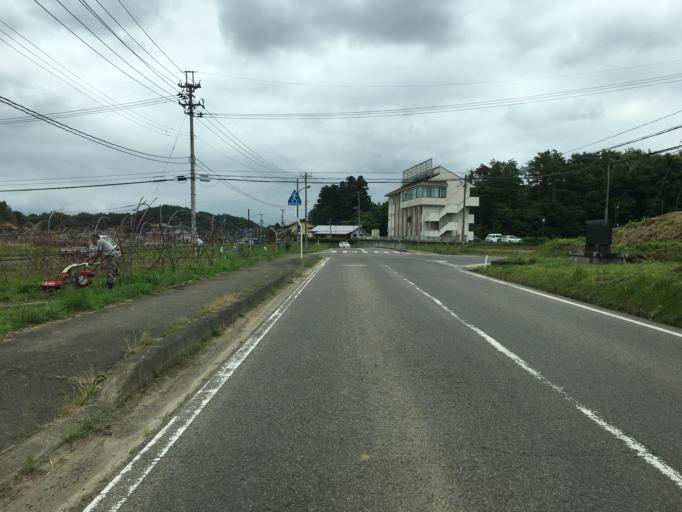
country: JP
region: Fukushima
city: Nihommatsu
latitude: 37.5786
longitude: 140.4274
